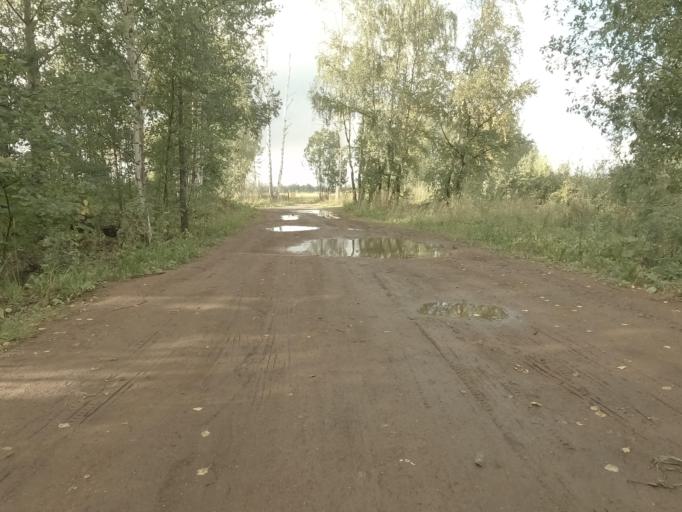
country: RU
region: St.-Petersburg
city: Krasnogvargeisky
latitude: 59.9755
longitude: 30.4905
